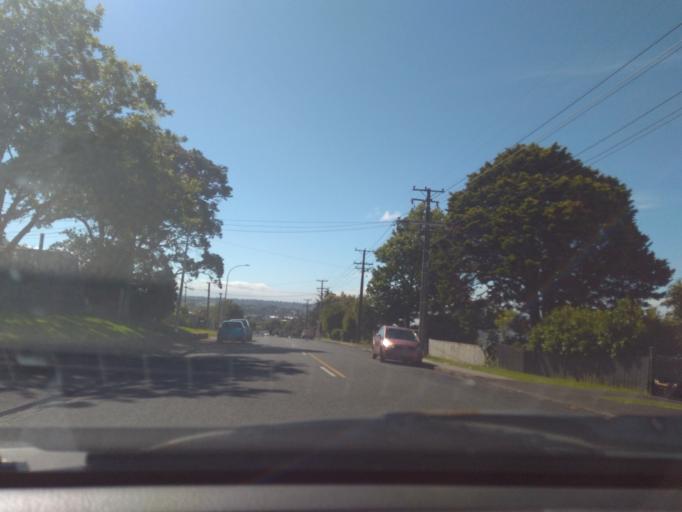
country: NZ
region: Auckland
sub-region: Auckland
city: Waitakere
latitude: -36.8974
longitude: 174.6425
